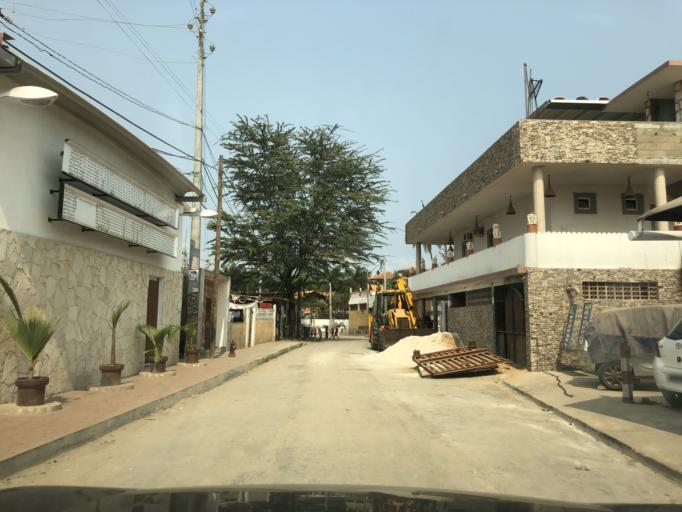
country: AO
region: Luanda
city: Luanda
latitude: -8.9033
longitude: 13.1642
